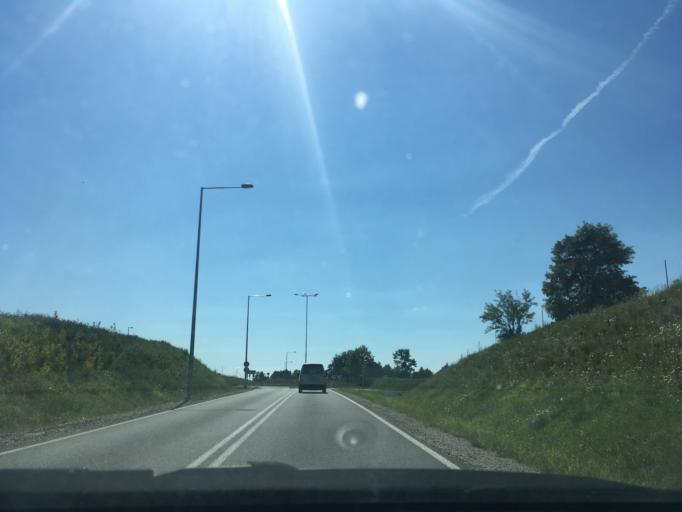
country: PL
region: Podlasie
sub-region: Powiat suwalski
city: Raczki
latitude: 53.9128
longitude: 22.8351
